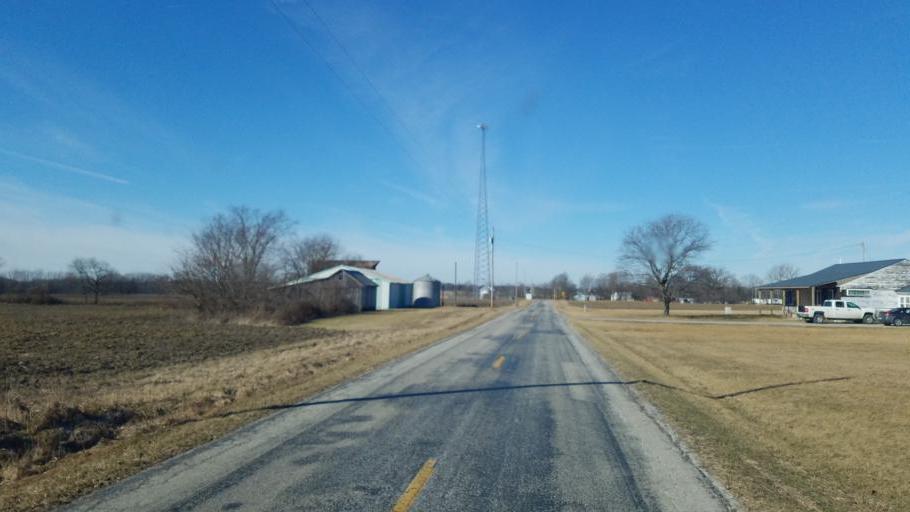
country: US
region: Ohio
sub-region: Union County
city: Richwood
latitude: 40.5147
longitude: -83.3194
